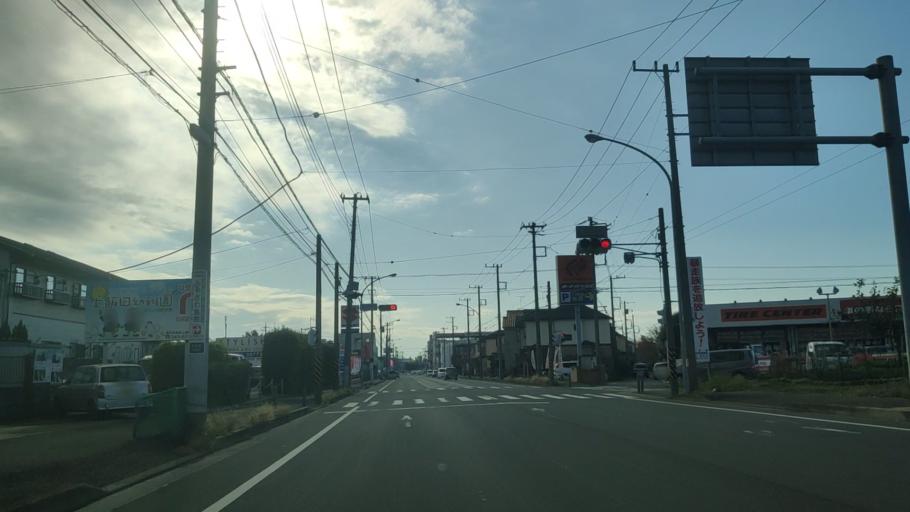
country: JP
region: Kanagawa
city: Minami-rinkan
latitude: 35.4258
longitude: 139.4840
